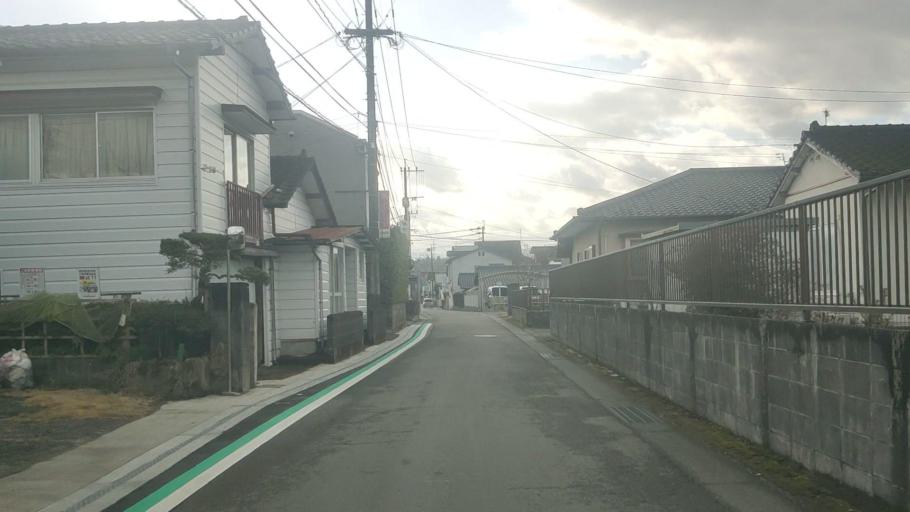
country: JP
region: Kumamoto
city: Hitoyoshi
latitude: 32.2207
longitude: 130.7715
